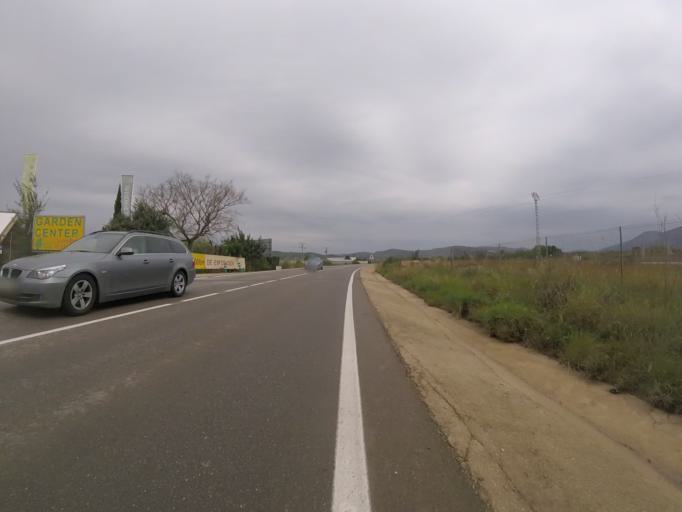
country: ES
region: Valencia
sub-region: Provincia de Castello
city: Alcoceber
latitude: 40.2522
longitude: 0.2464
